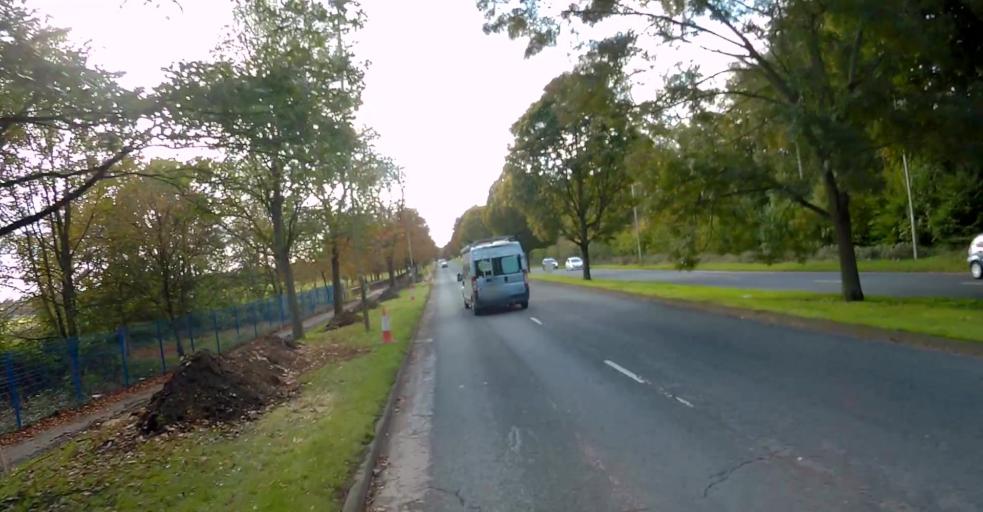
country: GB
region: England
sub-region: Hampshire
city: Aldershot
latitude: 51.2710
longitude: -0.7587
